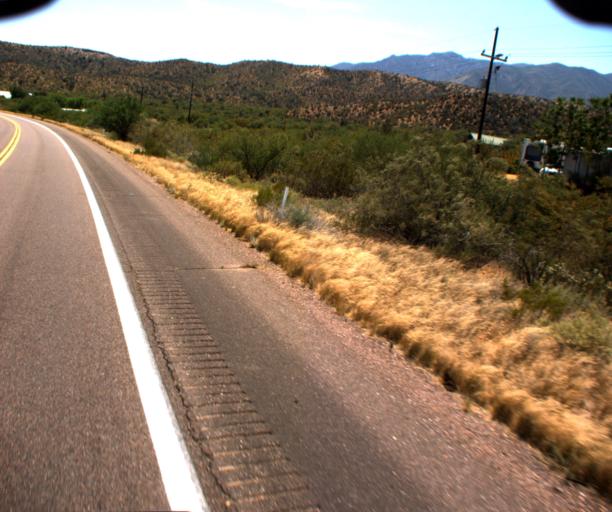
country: US
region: Arizona
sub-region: Gila County
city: Tonto Basin
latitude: 33.9627
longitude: -111.3255
